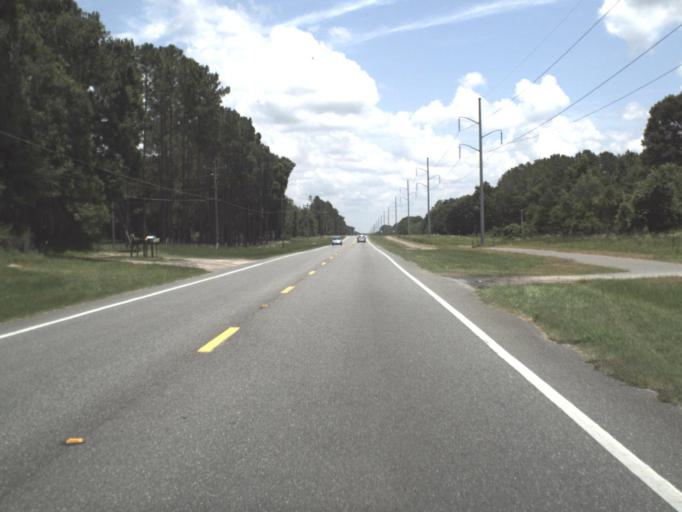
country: US
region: Florida
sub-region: Alachua County
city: Archer
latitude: 29.5530
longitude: -82.4934
